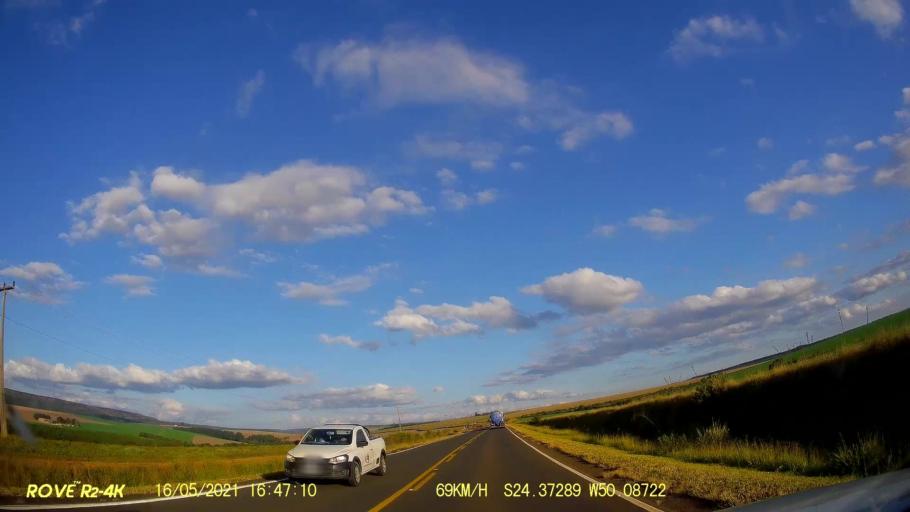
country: BR
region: Parana
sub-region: Pirai Do Sul
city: Pirai do Sul
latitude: -24.3732
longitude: -50.0867
